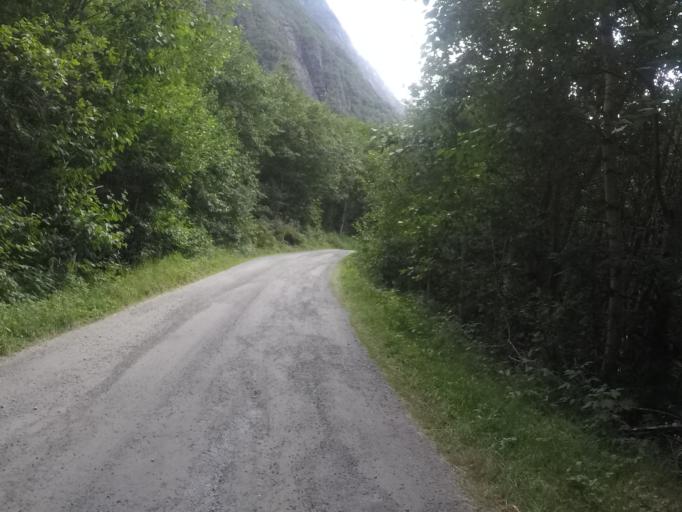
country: NO
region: Sogn og Fjordane
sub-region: Stryn
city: Stryn
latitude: 61.7623
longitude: 7.0416
